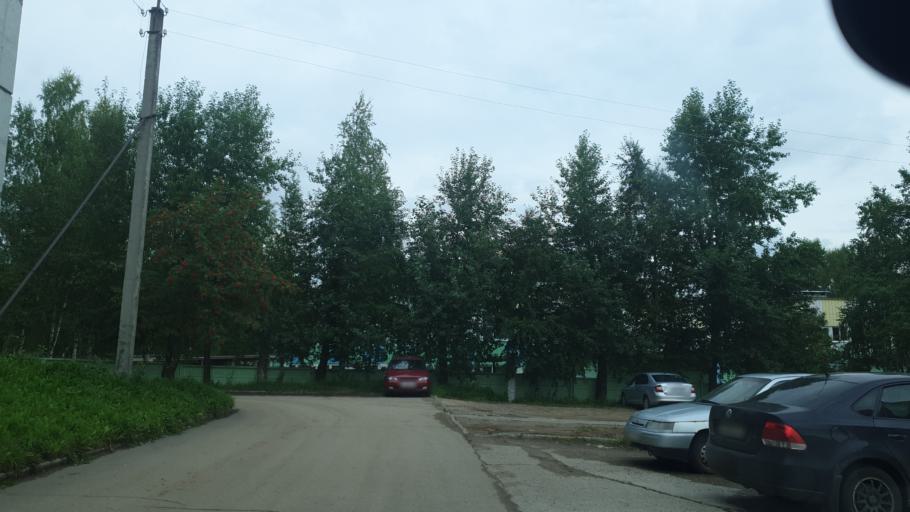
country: RU
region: Komi Republic
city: Ezhva
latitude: 61.7833
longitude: 50.7565
